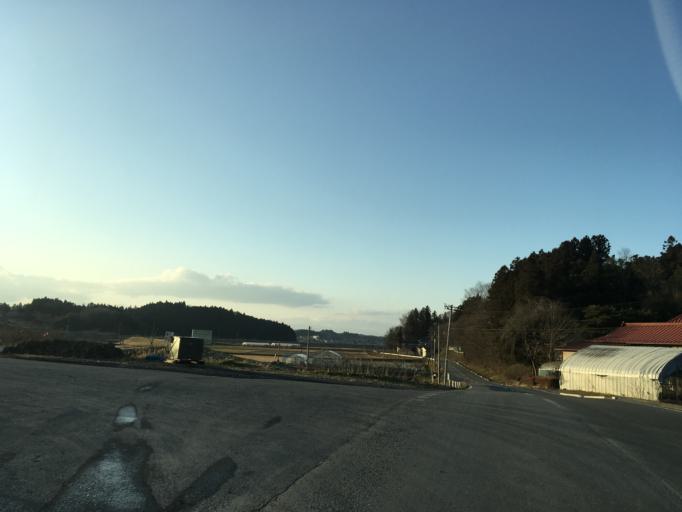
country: JP
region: Iwate
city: Ichinoseki
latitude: 38.8068
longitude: 141.2199
